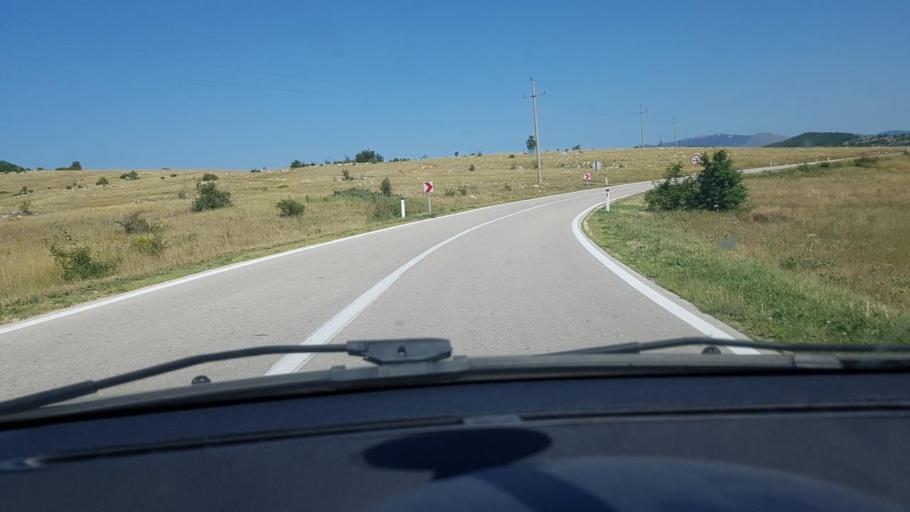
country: BA
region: Federation of Bosnia and Herzegovina
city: Bosansko Grahovo
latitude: 44.1334
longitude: 16.4767
